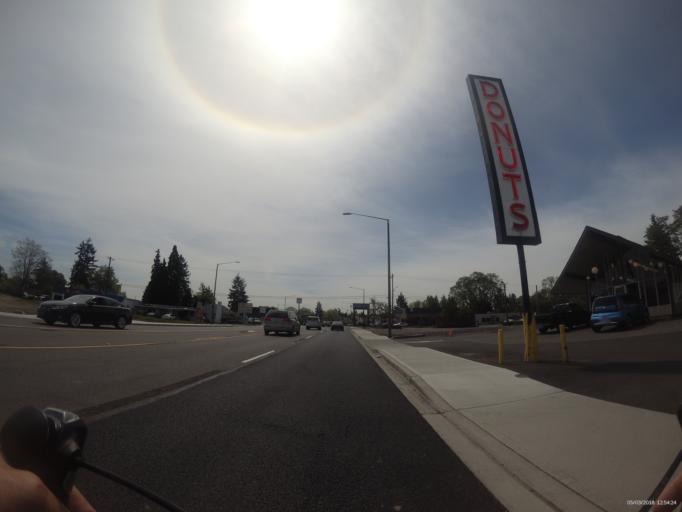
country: US
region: Washington
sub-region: Pierce County
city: Lakewood
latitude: 47.1690
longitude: -122.5202
